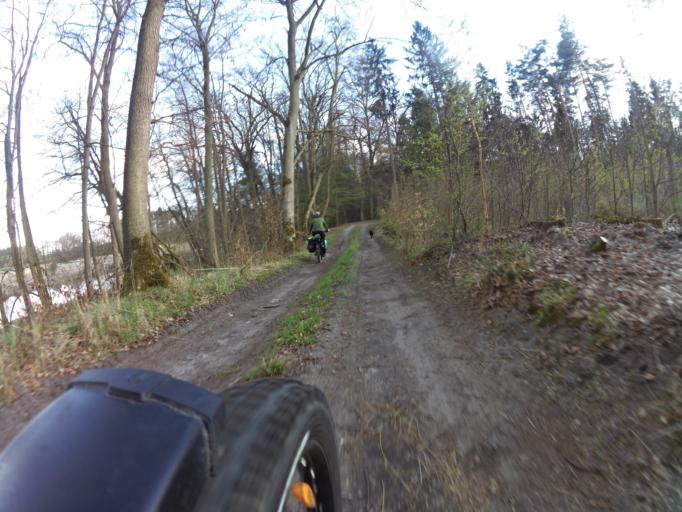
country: PL
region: West Pomeranian Voivodeship
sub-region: Powiat gryficki
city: Ploty
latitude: 53.7545
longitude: 15.2698
